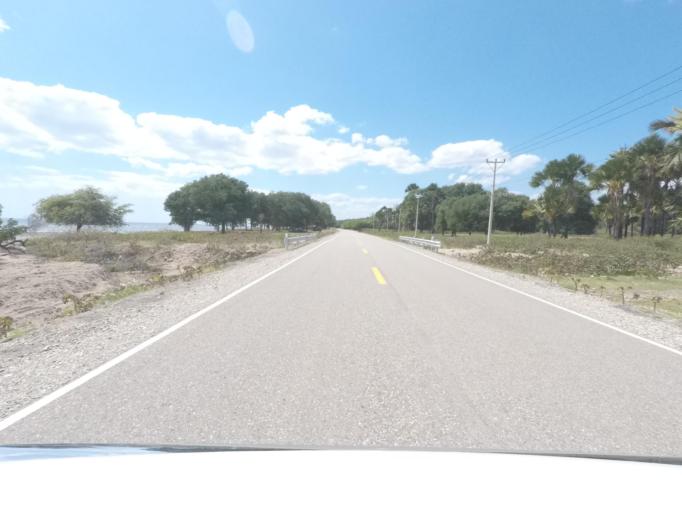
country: TL
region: Lautem
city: Lospalos
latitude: -8.4226
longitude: 126.7676
